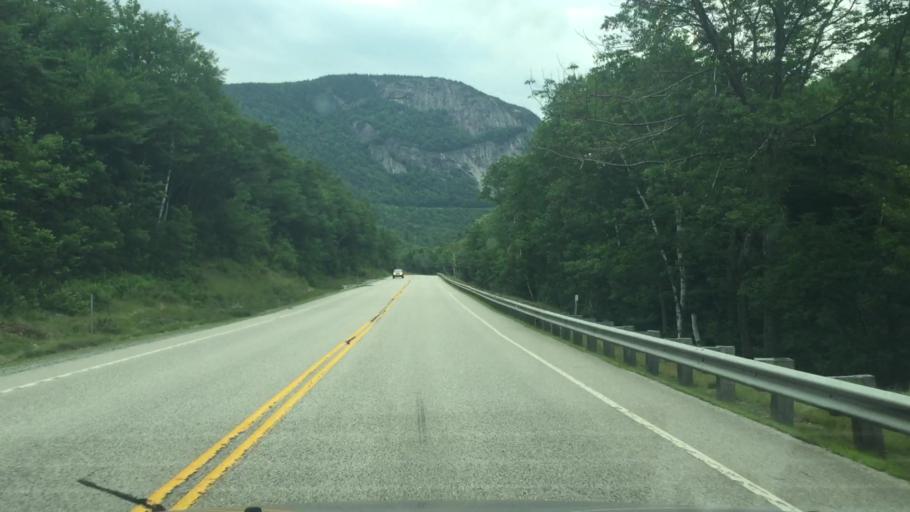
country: US
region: New Hampshire
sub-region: Grafton County
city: Deerfield
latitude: 44.1863
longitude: -71.4016
